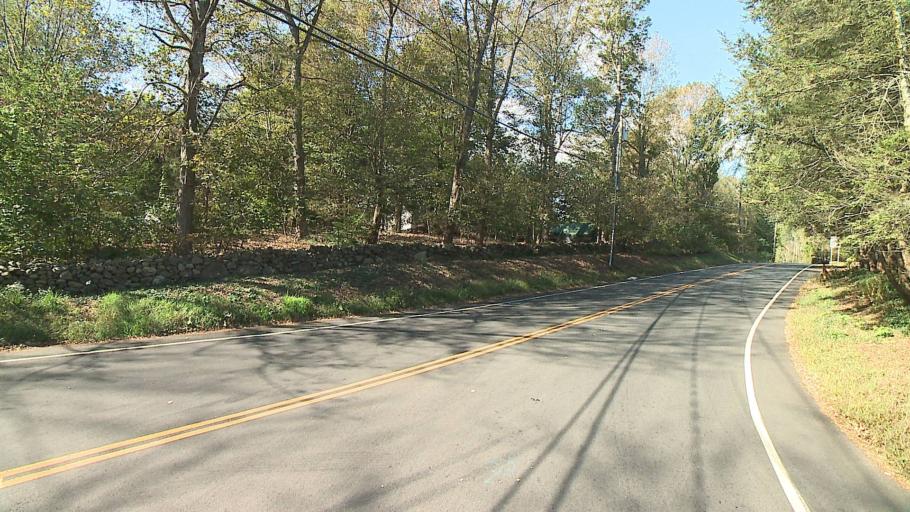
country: US
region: Connecticut
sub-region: New Haven County
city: Cheshire
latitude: 41.4729
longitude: -72.9323
